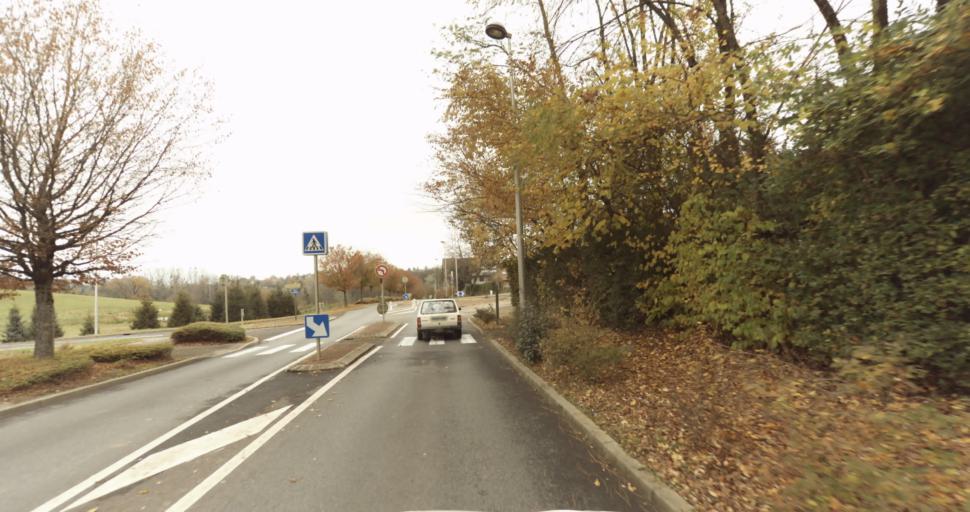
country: FR
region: Rhone-Alpes
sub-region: Departement de la Haute-Savoie
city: Seynod
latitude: 45.8634
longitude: 6.0833
